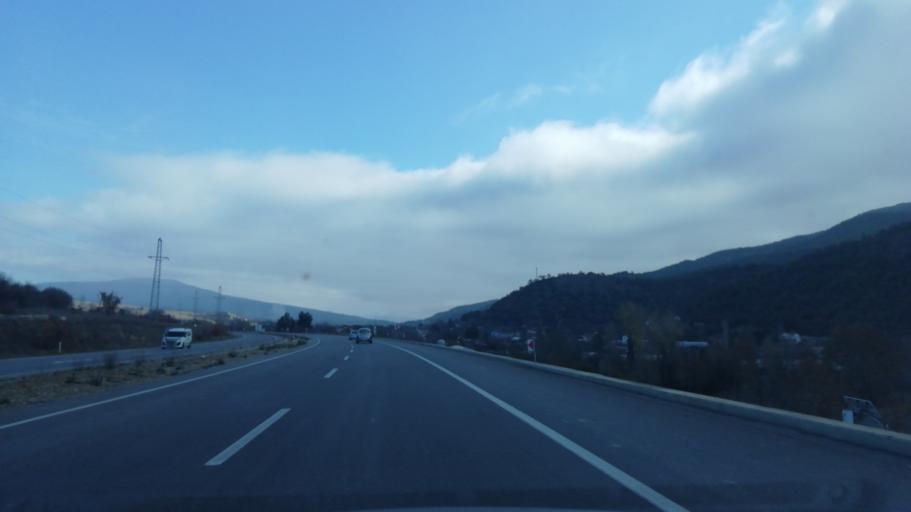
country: TR
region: Karabuk
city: Safranbolu
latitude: 41.2168
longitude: 32.7332
